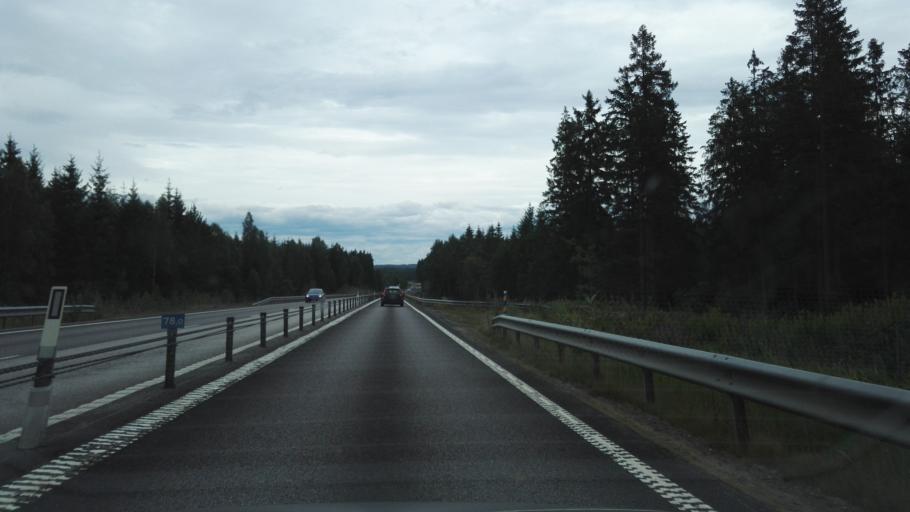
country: SE
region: Kronoberg
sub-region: Vaxjo Kommun
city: Rottne
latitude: 56.9627
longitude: 14.9543
